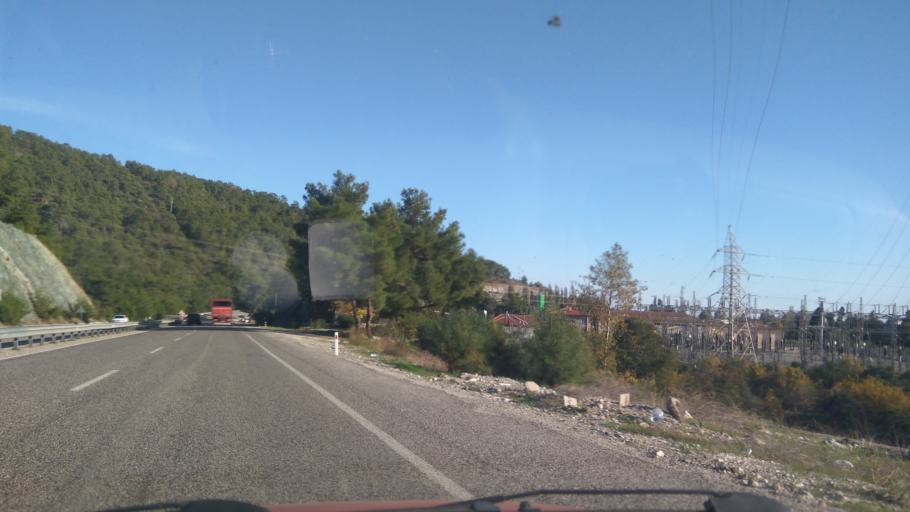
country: TR
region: Antalya
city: Kemer
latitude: 36.5823
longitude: 30.5488
